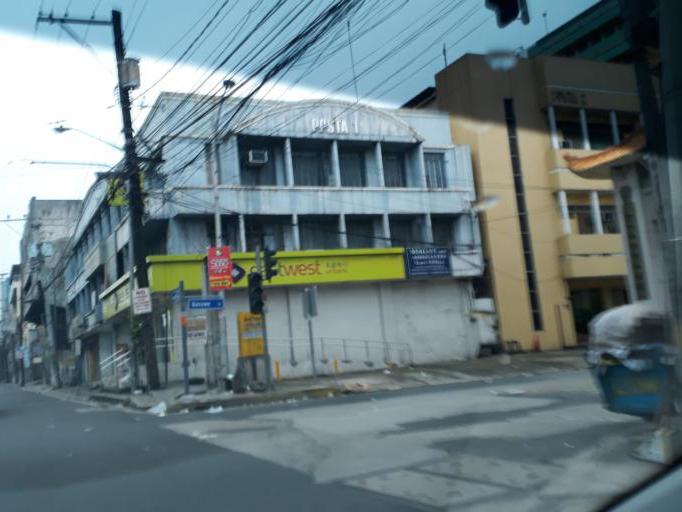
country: PH
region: Calabarzon
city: Del Monte
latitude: 14.6237
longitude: 121.0081
